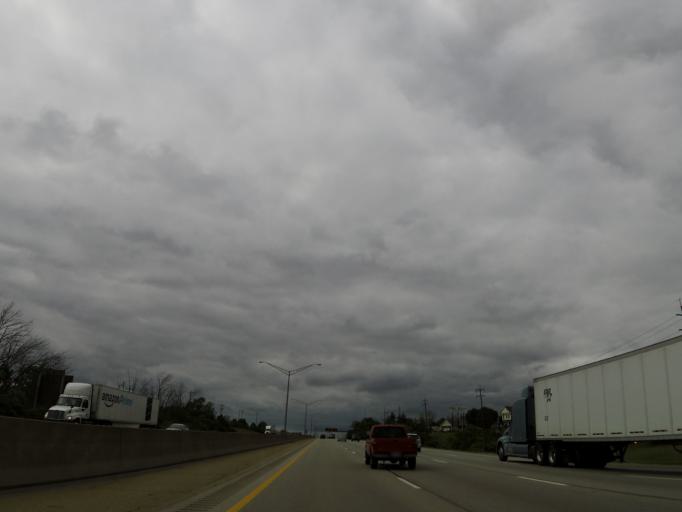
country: US
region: Kentucky
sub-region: Boone County
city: Walton
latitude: 38.9224
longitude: -84.6297
